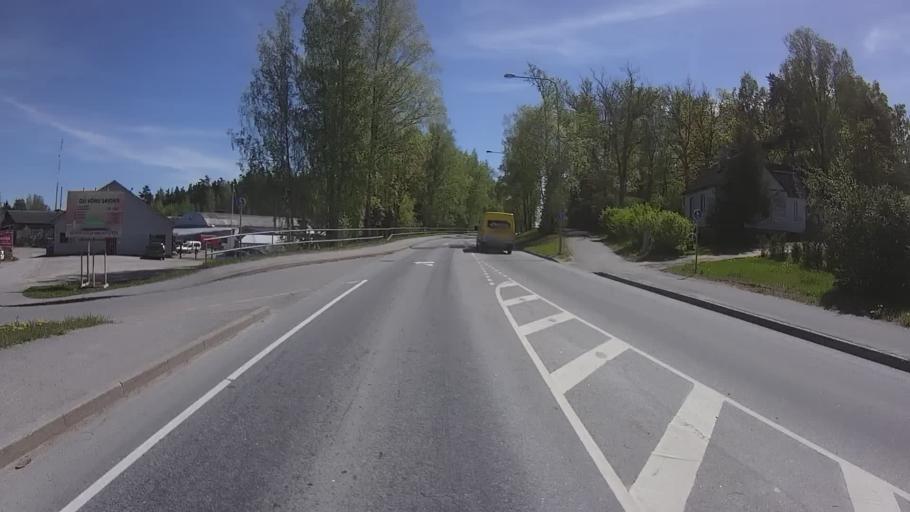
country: EE
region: Vorumaa
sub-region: Voru linn
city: Voru
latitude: 57.8263
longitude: 27.0139
